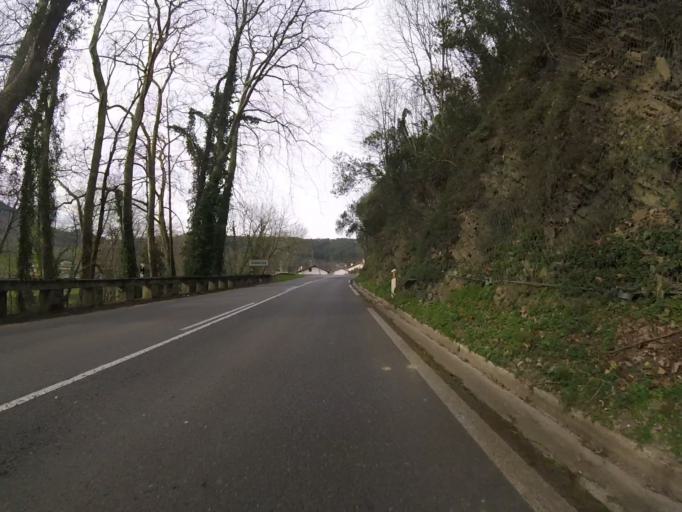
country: ES
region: Basque Country
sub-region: Provincia de Guipuzcoa
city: Aizarnazabal
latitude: 43.2594
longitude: -2.2345
